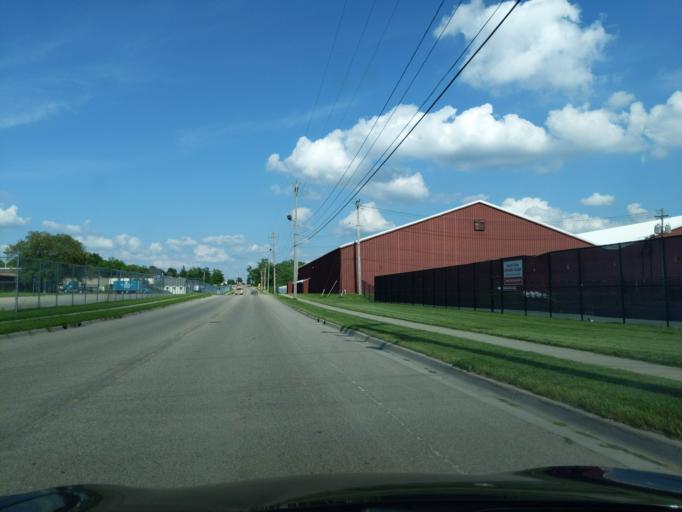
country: US
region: Michigan
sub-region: Ingham County
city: Lansing
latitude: 42.7627
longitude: -84.5288
